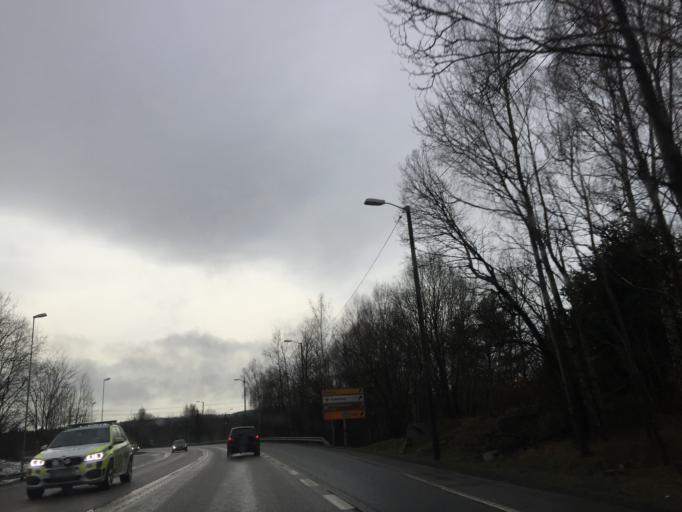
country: NO
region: Ostfold
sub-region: Moss
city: Moss
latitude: 59.4457
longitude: 10.6906
